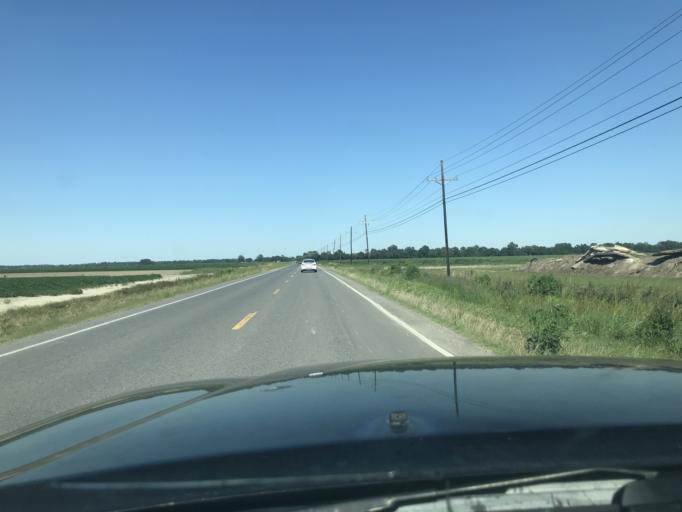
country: US
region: Louisiana
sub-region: West Baton Rouge Parish
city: Brusly
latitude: 30.4682
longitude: -91.3011
